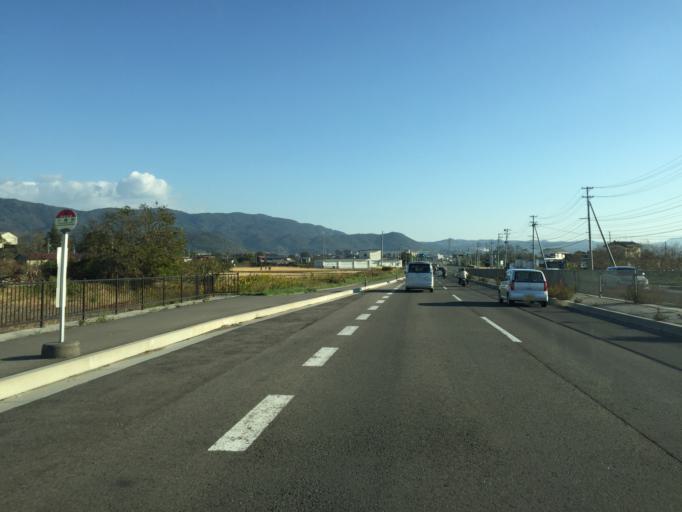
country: JP
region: Fukushima
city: Hobaramachi
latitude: 37.8608
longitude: 140.5259
